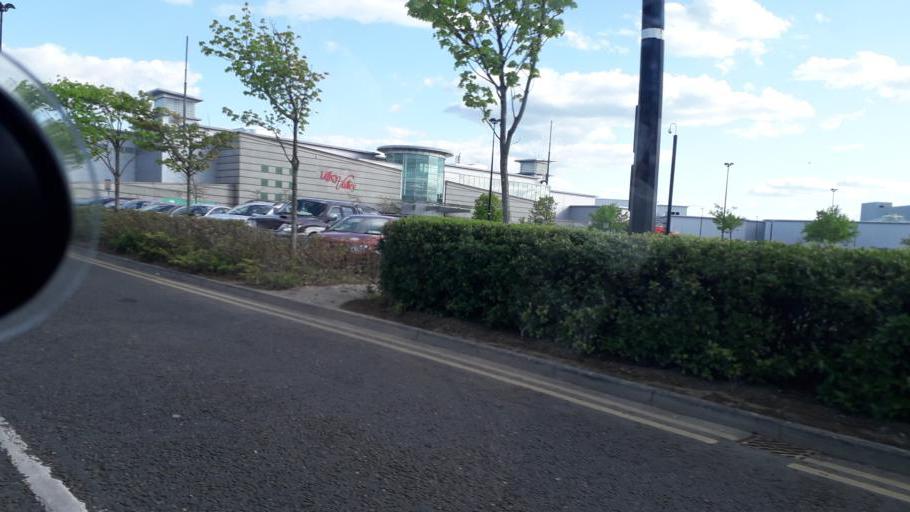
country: IE
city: Palmerstown
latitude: 53.3544
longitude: -6.3911
